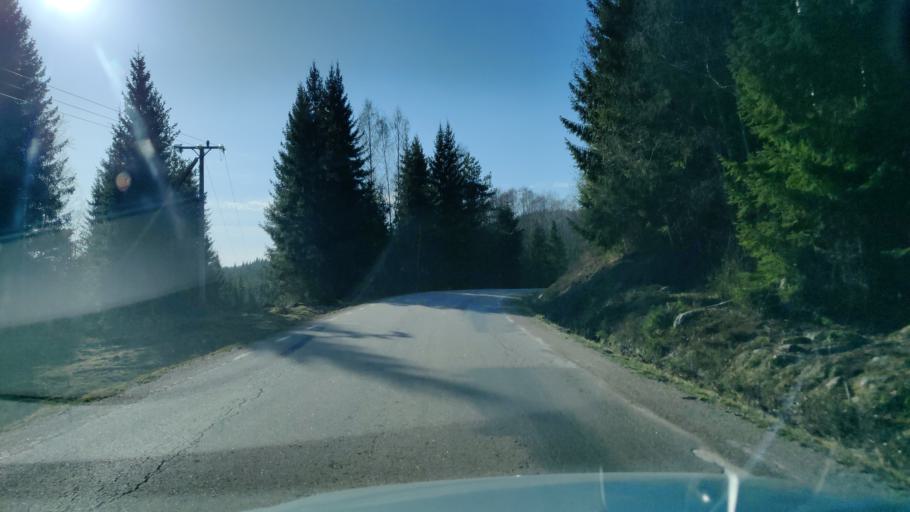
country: SE
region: Vaermland
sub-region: Munkfors Kommun
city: Munkfors
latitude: 59.9857
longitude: 13.3956
